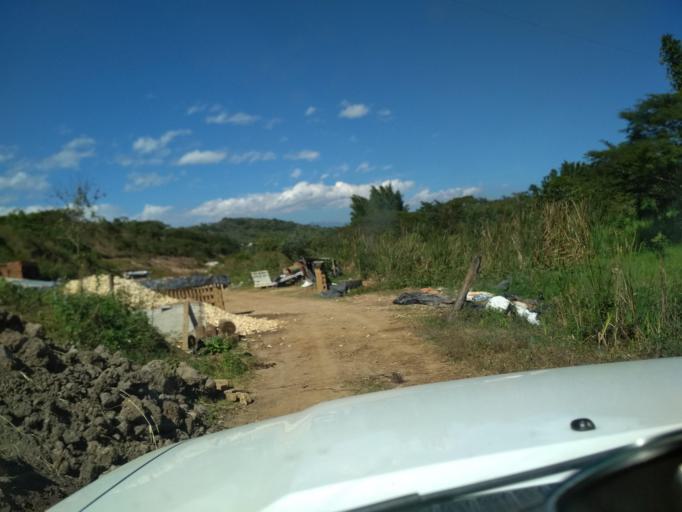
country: MX
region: Veracruz
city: El Castillo
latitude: 19.5463
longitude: -96.8531
